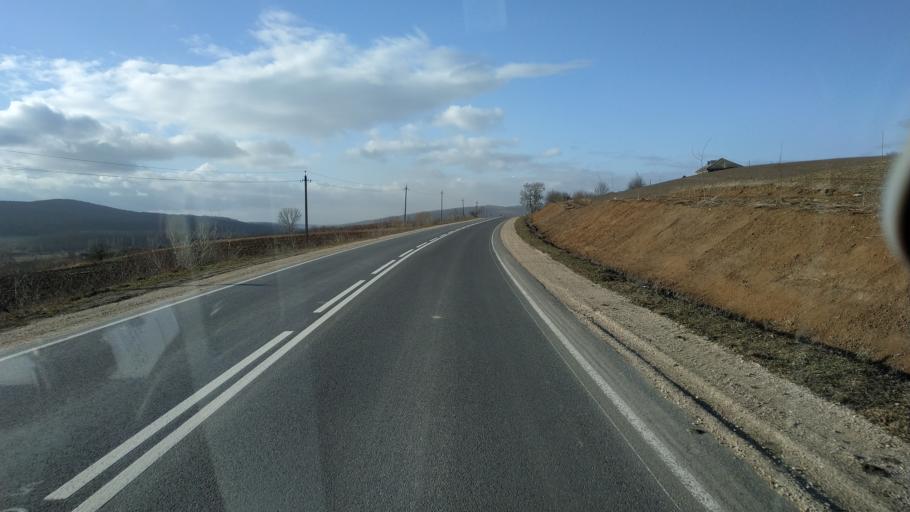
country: MD
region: Calarasi
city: Calarasi
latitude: 47.3134
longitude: 28.1192
